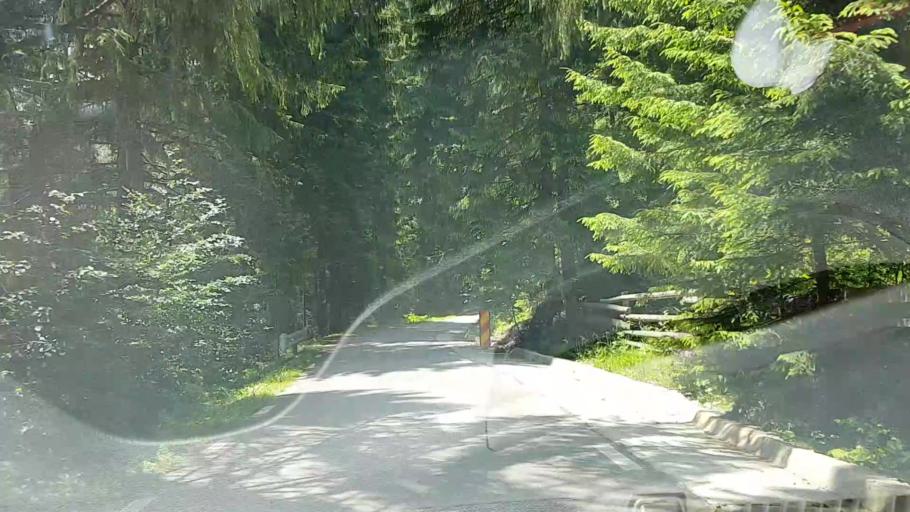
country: RO
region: Suceava
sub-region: Comuna Crucea
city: Crucea
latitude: 47.4265
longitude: 25.5798
